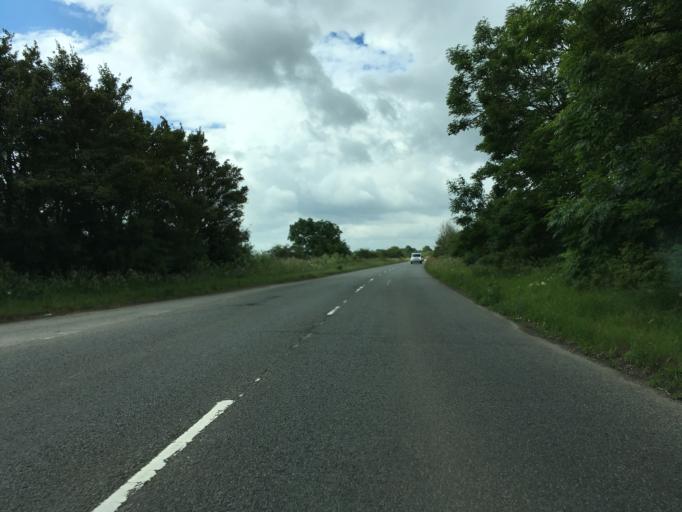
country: GB
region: England
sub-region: Borough of Swindon
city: Highworth
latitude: 51.6560
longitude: -1.7057
